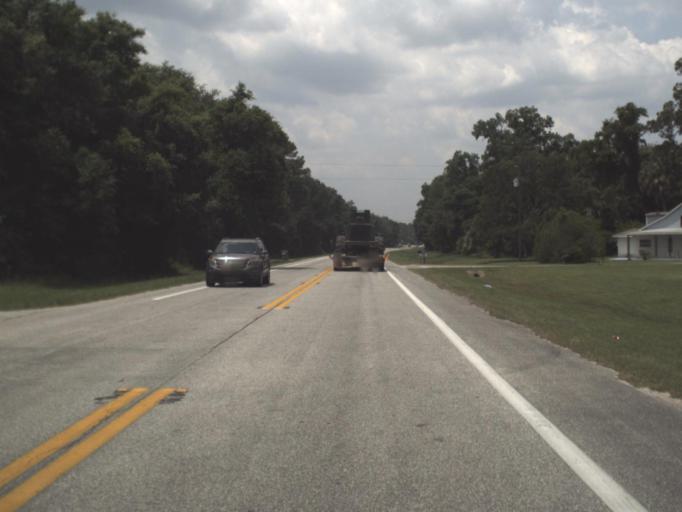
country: US
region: Florida
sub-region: Putnam County
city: Palatka
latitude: 29.6218
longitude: -81.6998
